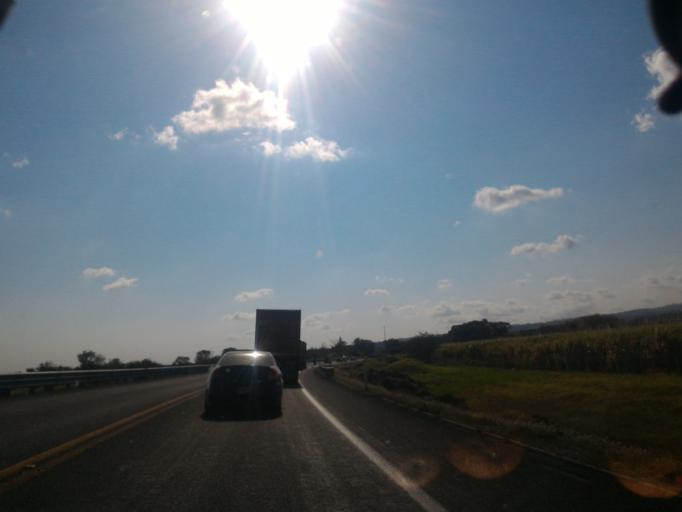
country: MX
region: Jalisco
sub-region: Tonila
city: San Marcos
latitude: 19.4360
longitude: -103.4811
